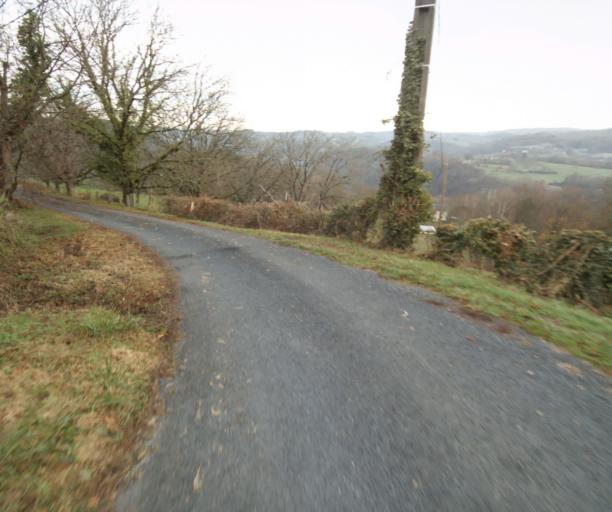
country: FR
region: Limousin
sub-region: Departement de la Correze
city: Chameyrat
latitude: 45.2310
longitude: 1.7044
